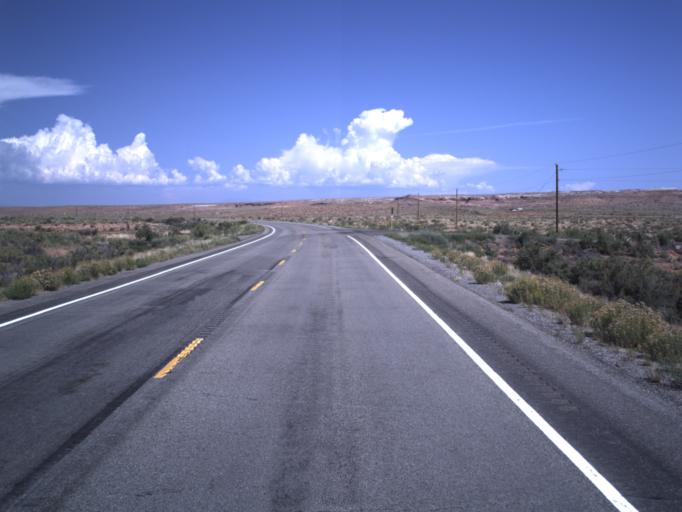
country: US
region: Utah
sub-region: San Juan County
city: Blanding
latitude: 37.1184
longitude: -109.5450
